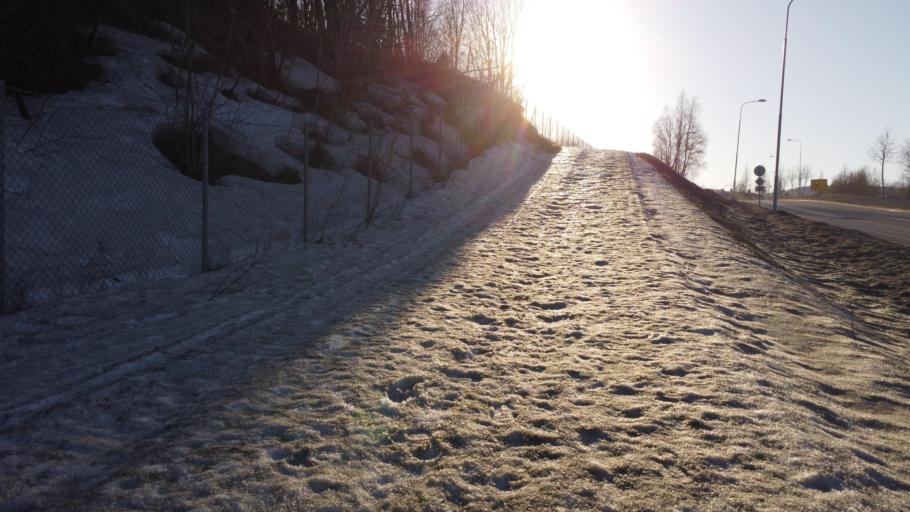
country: NO
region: Nordland
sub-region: Rana
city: Mo i Rana
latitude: 66.3142
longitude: 14.1636
